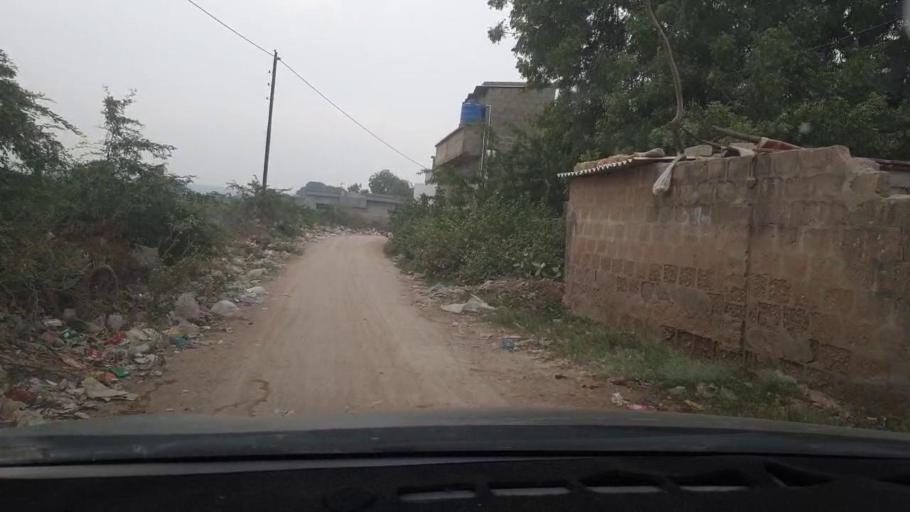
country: PK
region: Sindh
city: Malir Cantonment
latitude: 24.9224
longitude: 67.3184
